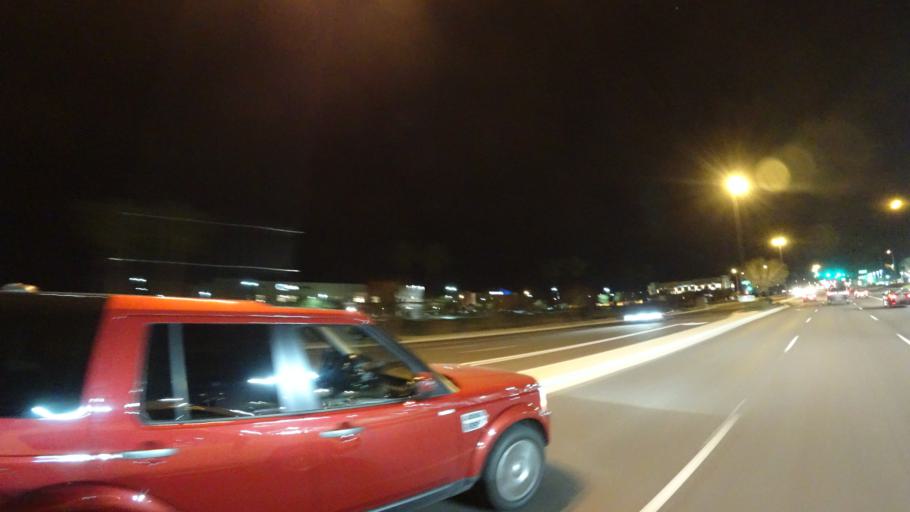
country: US
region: Arizona
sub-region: Maricopa County
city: Gilbert
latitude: 33.2938
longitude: -111.7557
